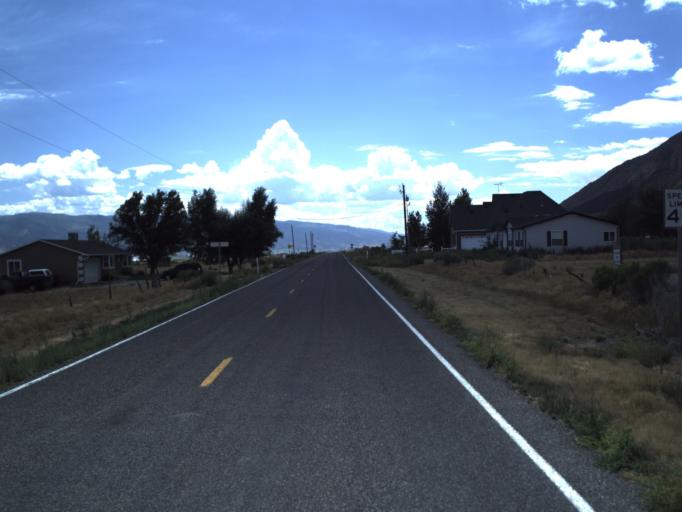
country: US
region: Utah
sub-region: Sanpete County
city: Moroni
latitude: 39.4808
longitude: -111.6351
